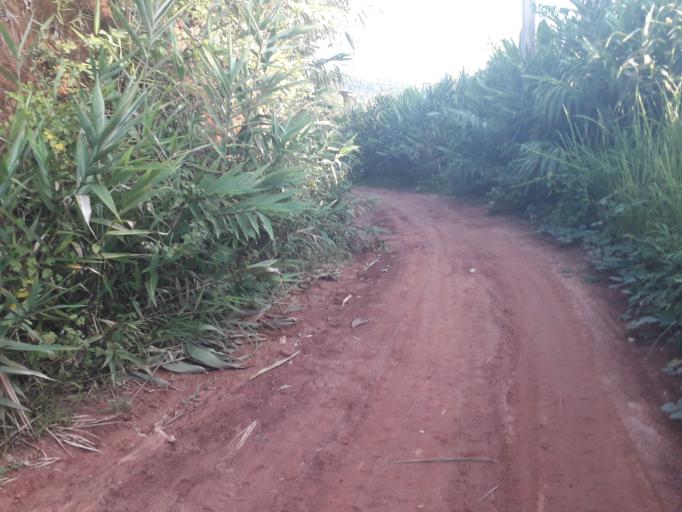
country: CN
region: Yunnan
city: Menglie
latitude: 22.1244
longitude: 101.7500
